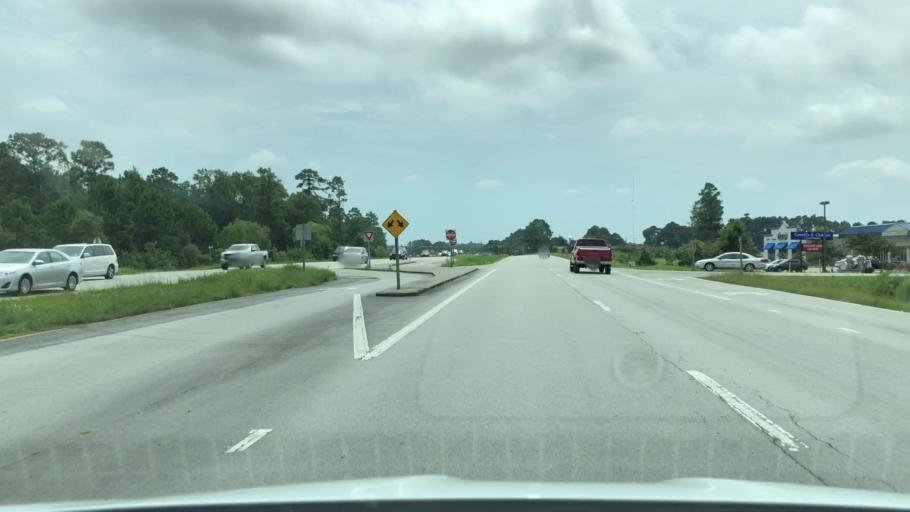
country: US
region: North Carolina
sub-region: Carteret County
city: Newport
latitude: 34.7938
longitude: -76.8774
